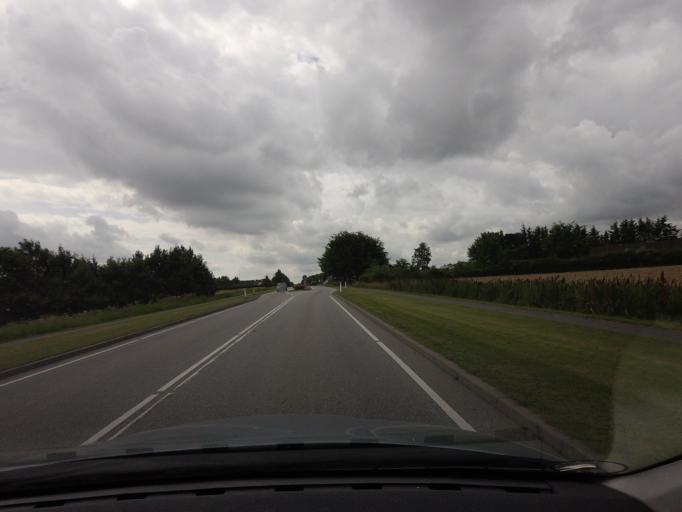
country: DK
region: North Denmark
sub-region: Hjorring Kommune
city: Hjorring
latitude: 57.4036
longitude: 9.9880
